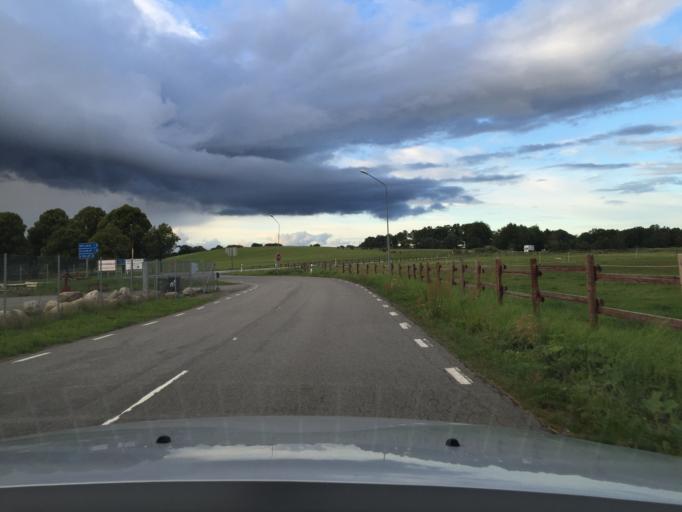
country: SE
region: Skane
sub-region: Hassleholms Kommun
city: Sosdala
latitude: 56.0513
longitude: 13.7196
